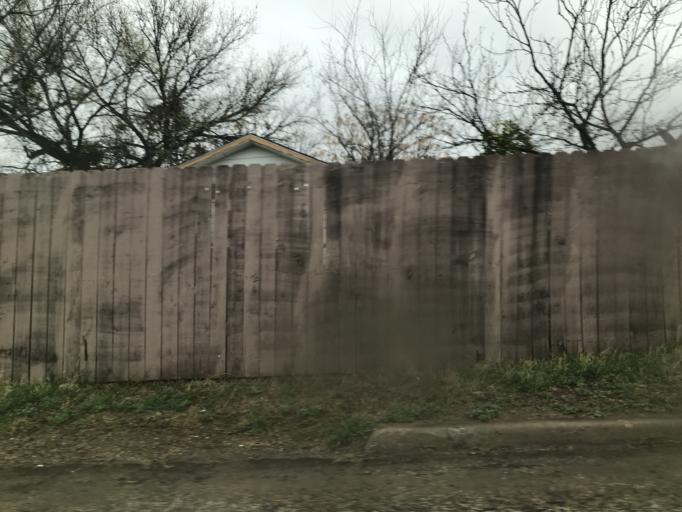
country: US
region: Texas
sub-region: Tom Green County
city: San Angelo
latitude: 31.4644
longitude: -100.4189
